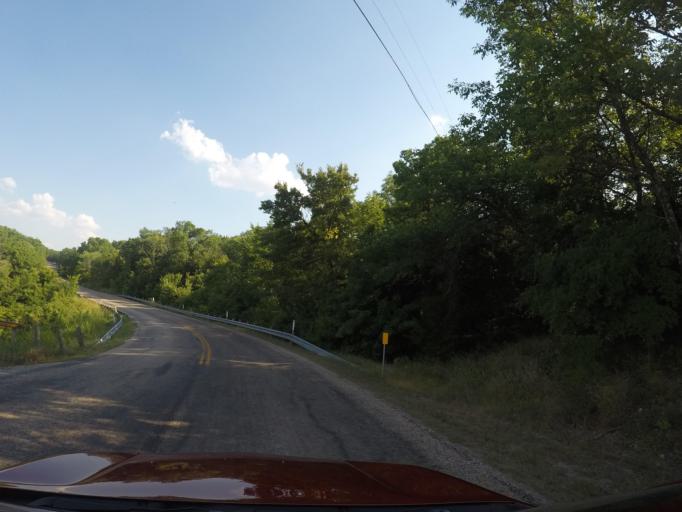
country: US
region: Texas
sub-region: Grayson County
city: Preston
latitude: 33.8136
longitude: -96.6095
